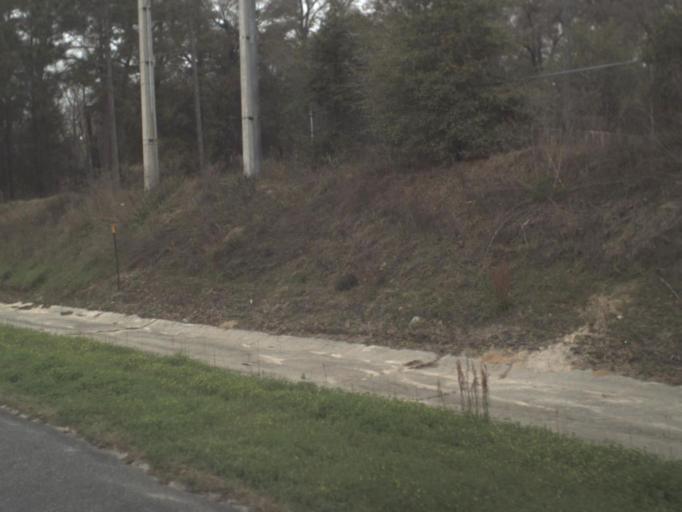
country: US
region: Florida
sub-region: Liberty County
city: Bristol
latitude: 30.3950
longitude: -84.7921
